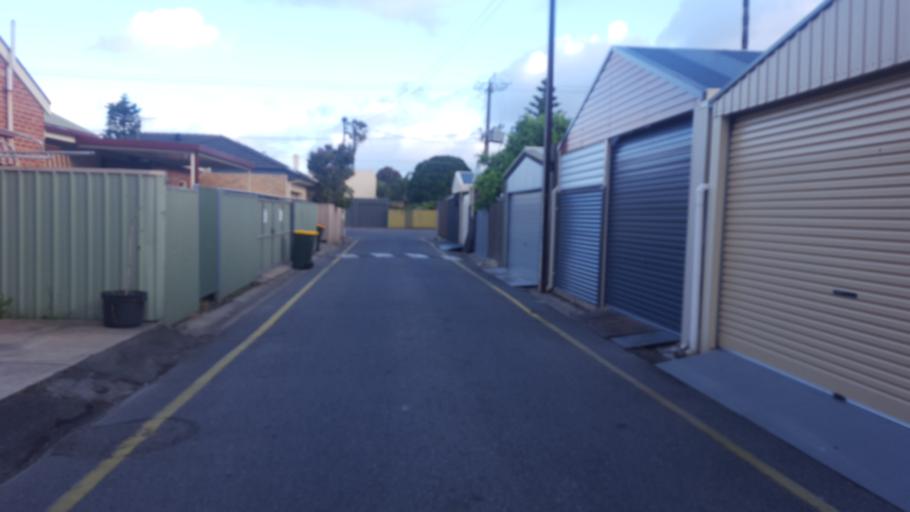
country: AU
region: South Australia
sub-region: Adelaide
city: Glenelg
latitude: -34.9788
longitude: 138.5171
